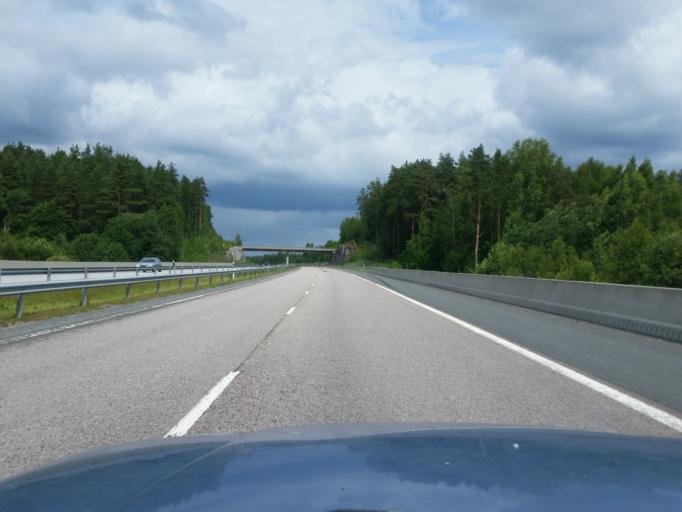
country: FI
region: Paijanne Tavastia
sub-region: Lahti
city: Nastola
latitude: 61.0081
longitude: 25.8131
